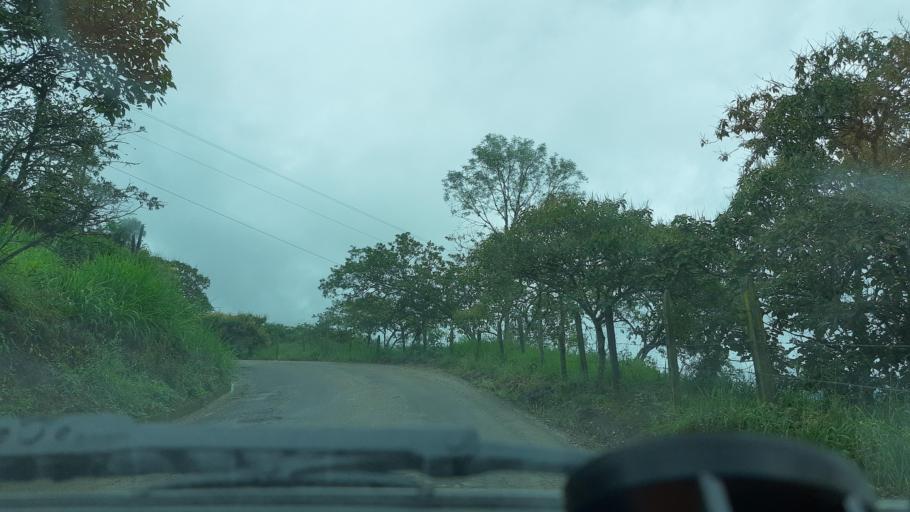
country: CO
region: Cundinamarca
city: Manta
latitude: 5.0426
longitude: -73.5141
